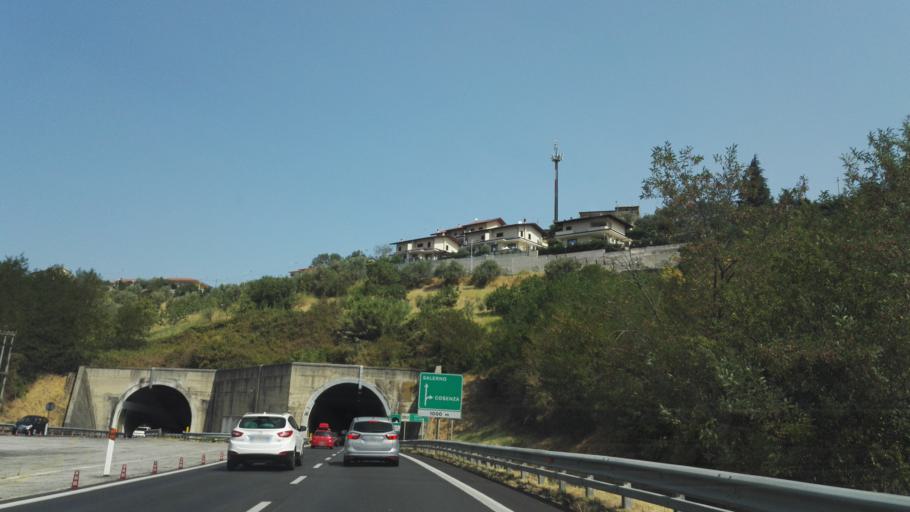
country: IT
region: Calabria
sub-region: Provincia di Cosenza
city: Rosario
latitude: 39.2912
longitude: 16.2389
